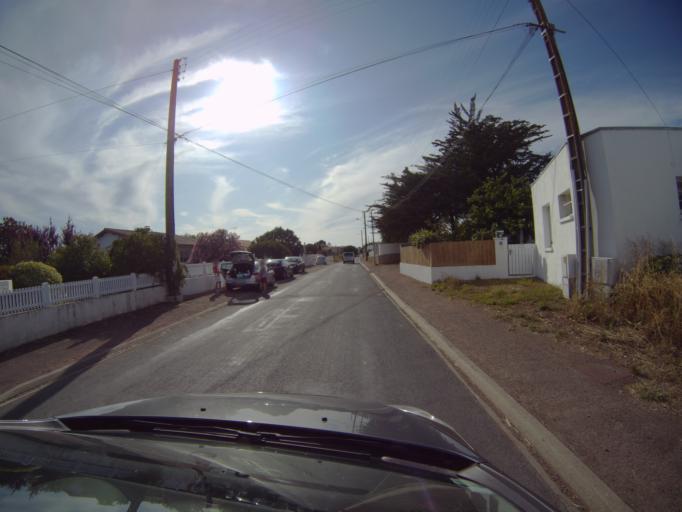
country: FR
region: Pays de la Loire
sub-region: Departement de la Vendee
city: Angles
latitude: 46.4051
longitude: -1.4076
